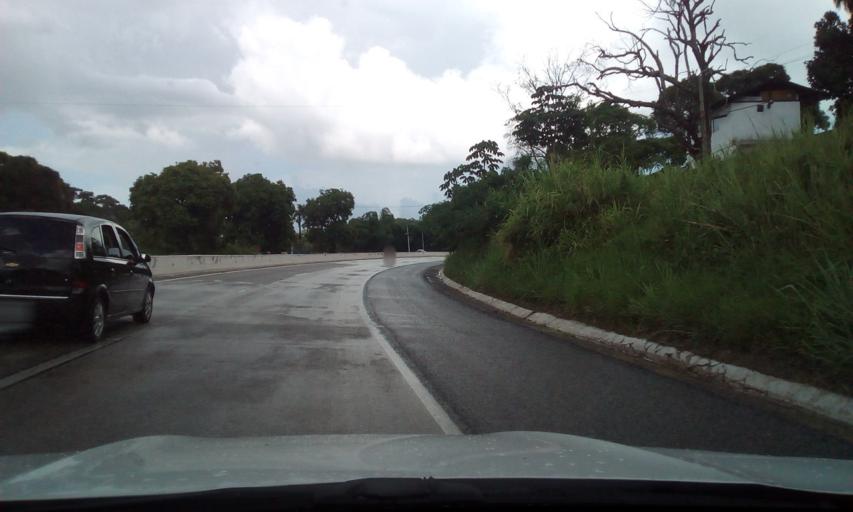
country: BR
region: Pernambuco
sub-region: Cabo De Santo Agostinho
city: Cabo
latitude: -8.3098
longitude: -35.0828
